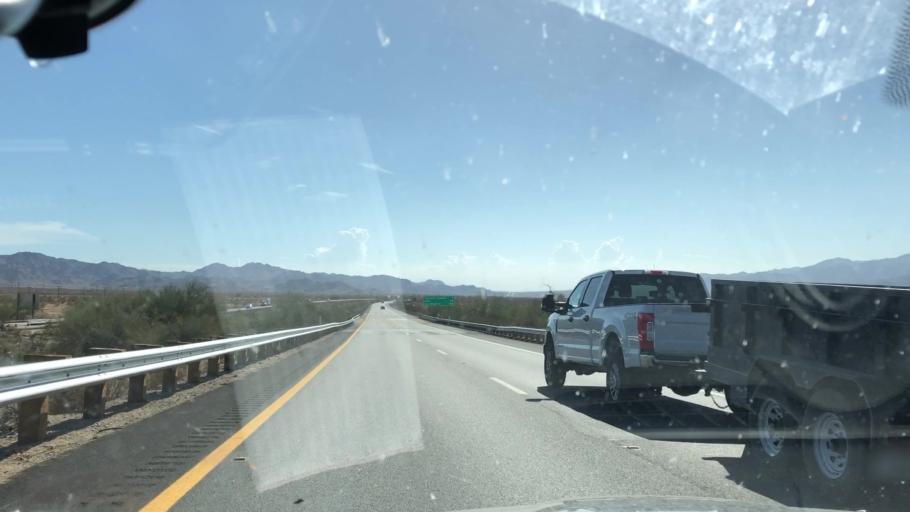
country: US
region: California
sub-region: Imperial County
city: Niland
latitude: 33.6756
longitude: -115.5732
